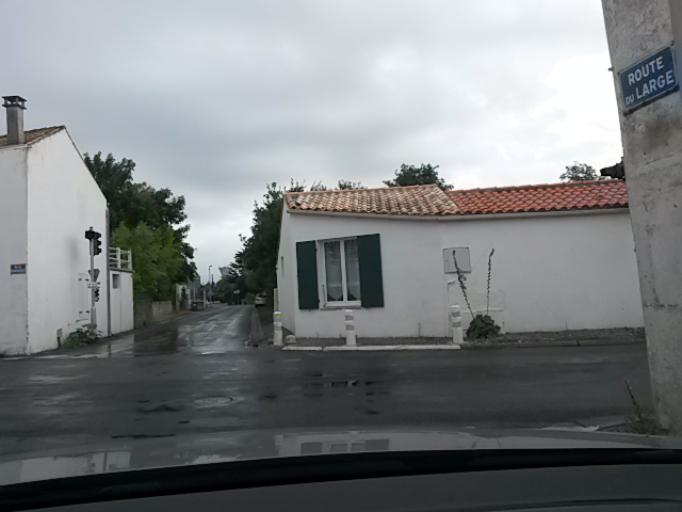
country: FR
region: Poitou-Charentes
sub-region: Departement de la Charente-Maritime
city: Dolus-d'Oleron
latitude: 45.8829
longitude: -1.2502
